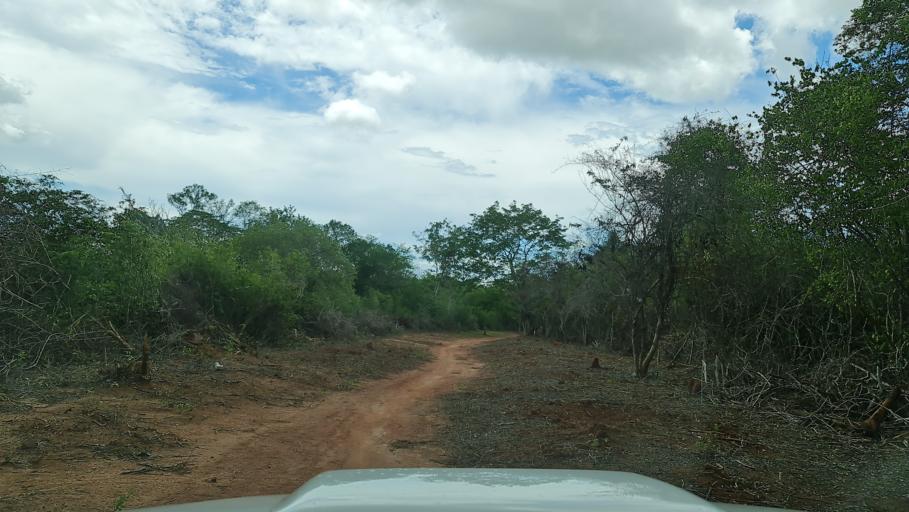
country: MZ
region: Nampula
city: Ilha de Mocambique
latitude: -15.5011
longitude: 40.1752
